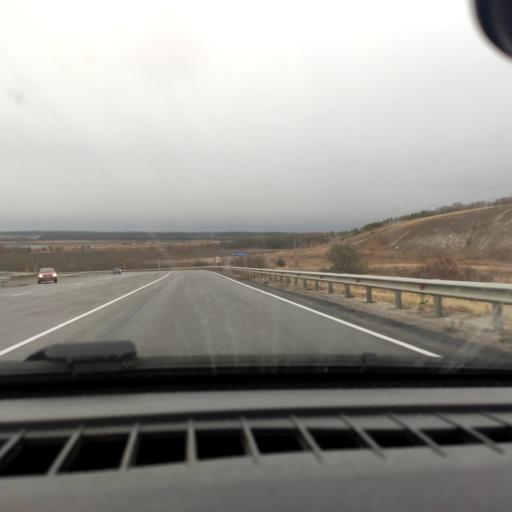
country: RU
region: Voronezj
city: Ostrogozhsk
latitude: 51.0248
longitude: 38.9851
